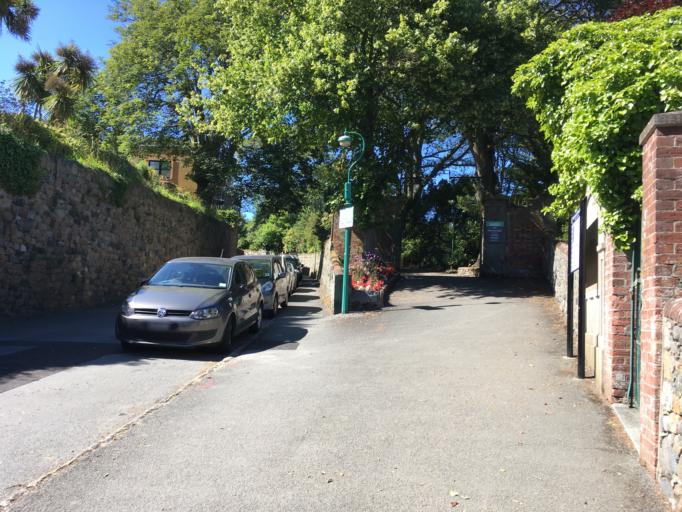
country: GG
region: St Peter Port
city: Saint Peter Port
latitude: 49.4577
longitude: -2.5392
